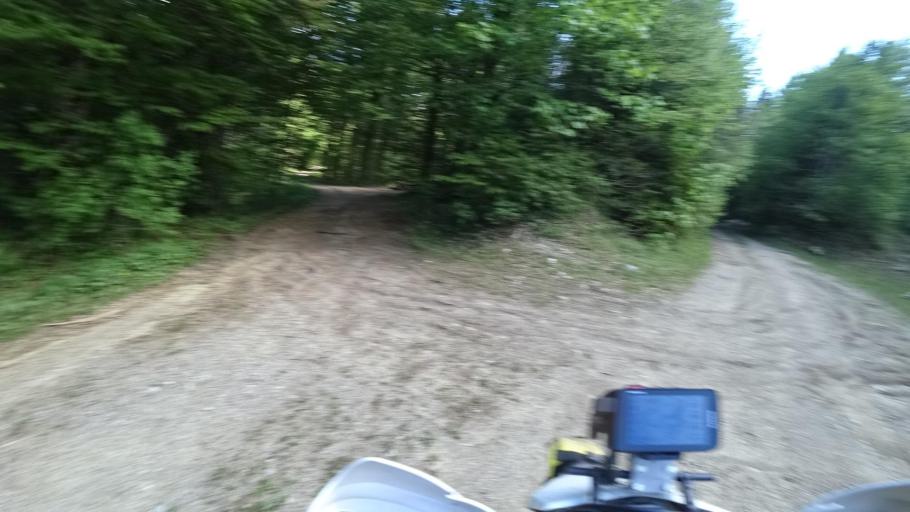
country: BA
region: Federation of Bosnia and Herzegovina
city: Orasac
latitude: 44.7337
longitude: 16.0918
